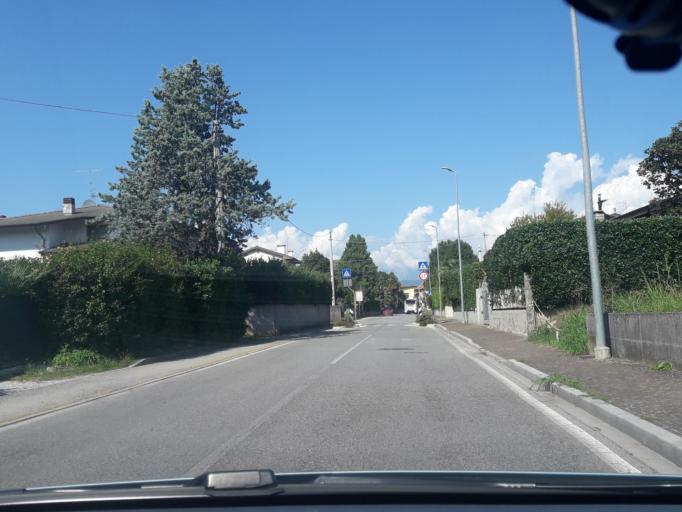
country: IT
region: Friuli Venezia Giulia
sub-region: Provincia di Udine
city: Colugna
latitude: 46.0990
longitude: 13.2084
